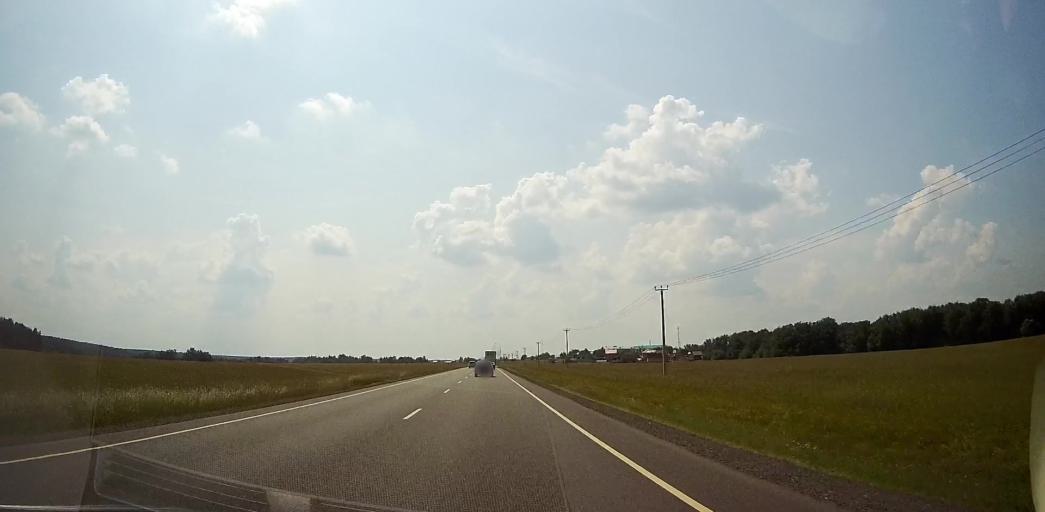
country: RU
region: Moskovskaya
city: Meshcherino
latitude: 55.1521
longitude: 38.3022
